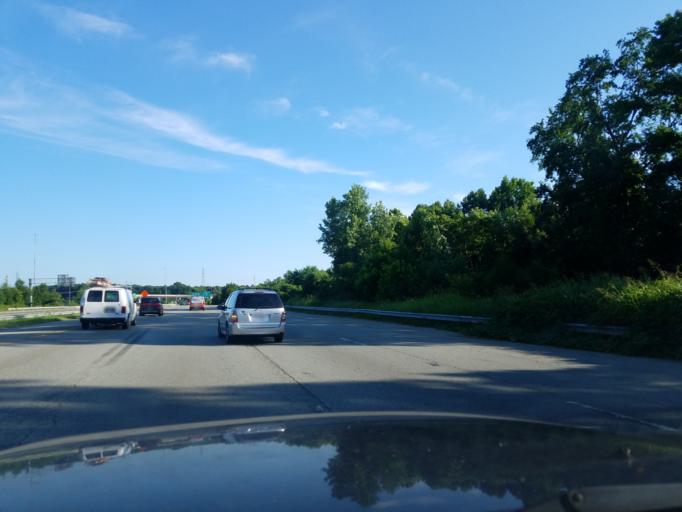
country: US
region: North Carolina
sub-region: Durham County
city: Durham
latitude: 36.0084
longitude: -78.8662
